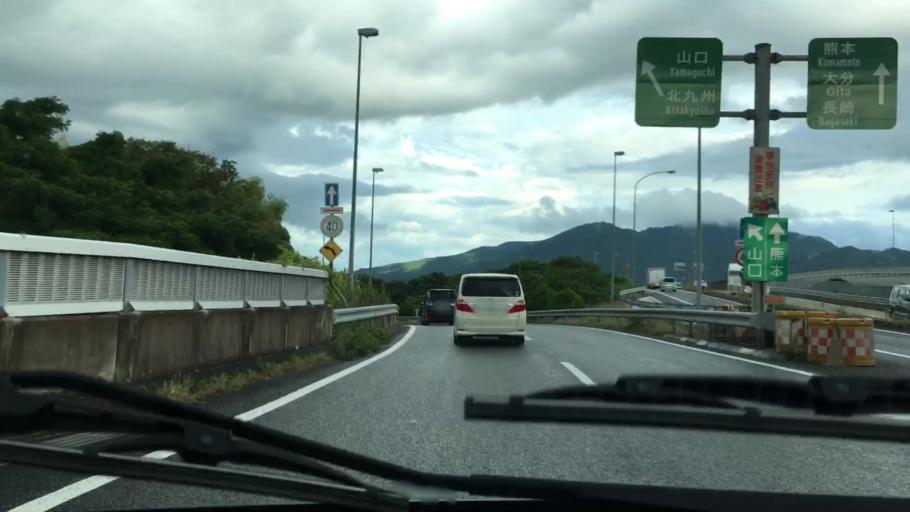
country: JP
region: Fukuoka
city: Sasaguri
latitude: 33.6300
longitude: 130.4880
